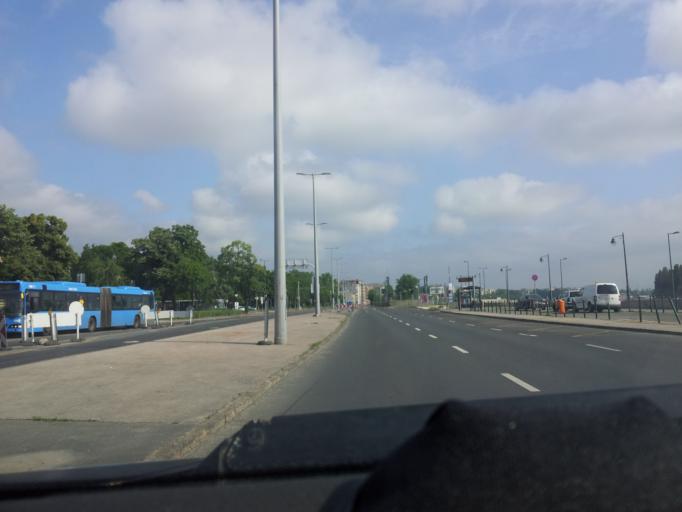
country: HU
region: Budapest
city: Budapest II. keruelet
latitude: 47.5154
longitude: 19.0395
